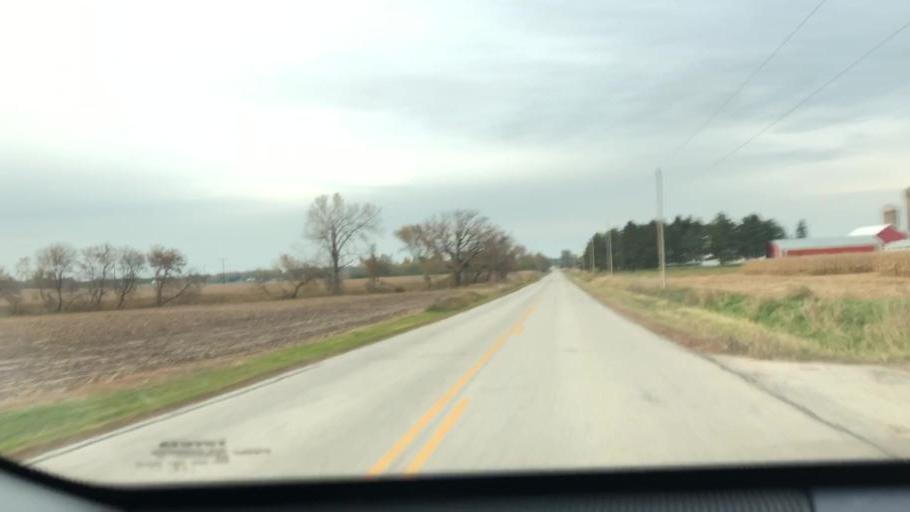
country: US
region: Wisconsin
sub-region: Outagamie County
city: Seymour
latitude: 44.4495
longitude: -88.3503
